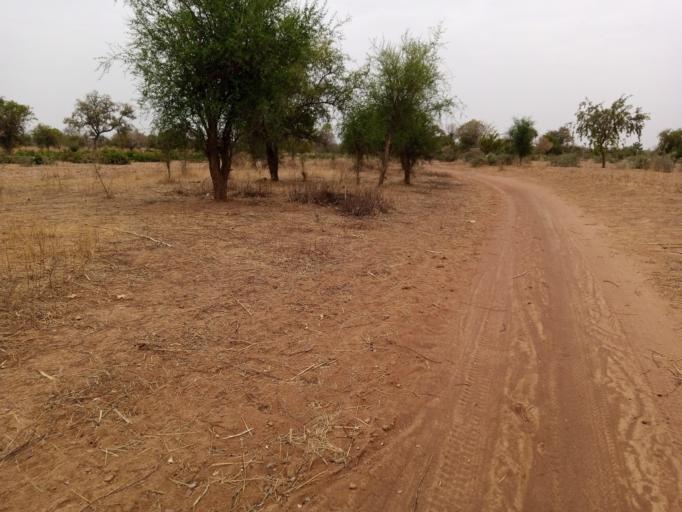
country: BF
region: Boucle du Mouhoun
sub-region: Province de la Kossi
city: Nouna
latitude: 12.8413
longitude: -4.0769
